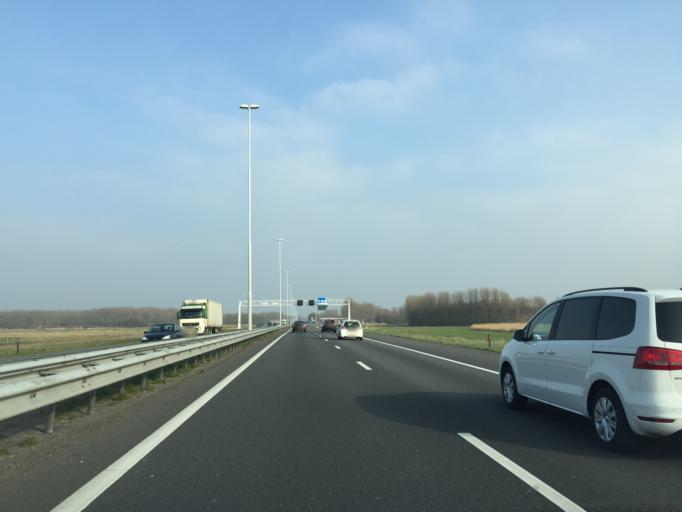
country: NL
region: South Holland
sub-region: Gemeente Vlaardingen
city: Vlaardingen
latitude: 51.9207
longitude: 4.2992
